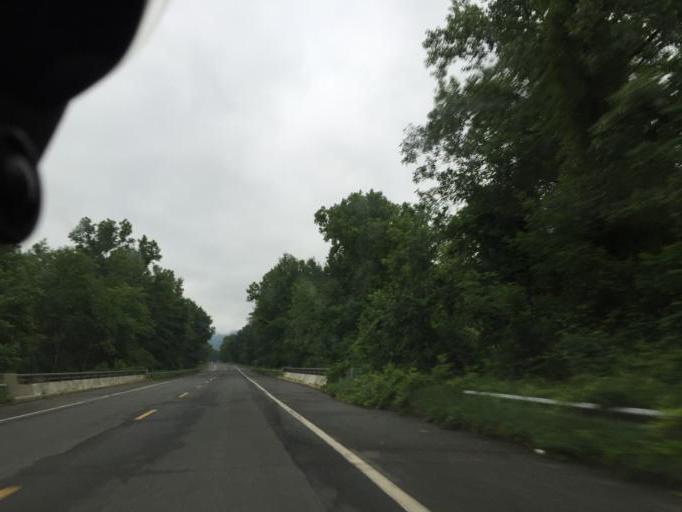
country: US
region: Connecticut
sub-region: Litchfield County
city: Canaan
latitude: 42.0539
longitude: -73.3268
